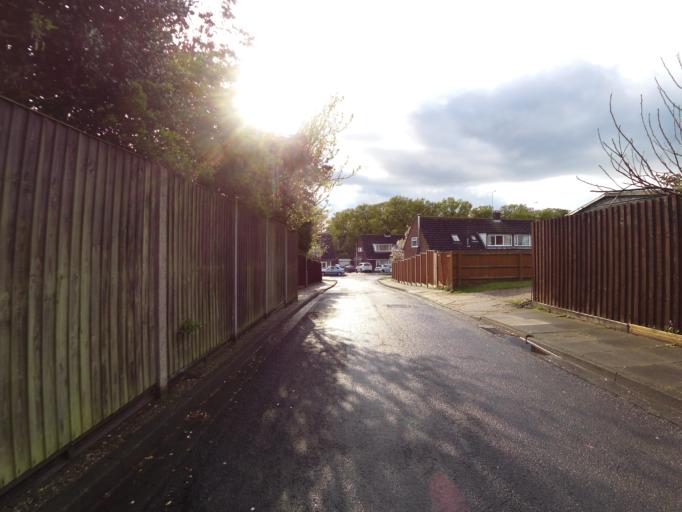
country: GB
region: England
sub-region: Suffolk
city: Kesgrave
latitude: 52.0466
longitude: 1.1977
